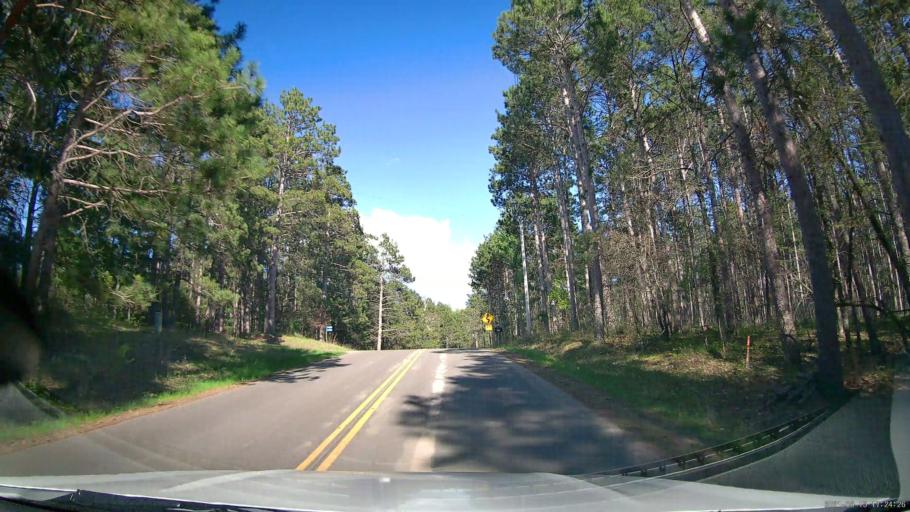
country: US
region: Minnesota
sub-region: Hubbard County
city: Park Rapids
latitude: 46.9925
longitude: -94.9591
